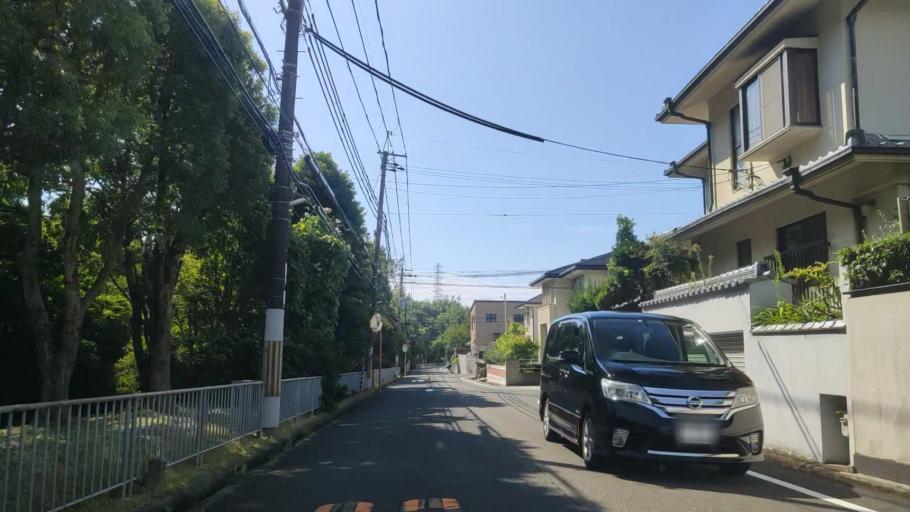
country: JP
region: Osaka
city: Ibaraki
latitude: 34.8172
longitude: 135.5190
